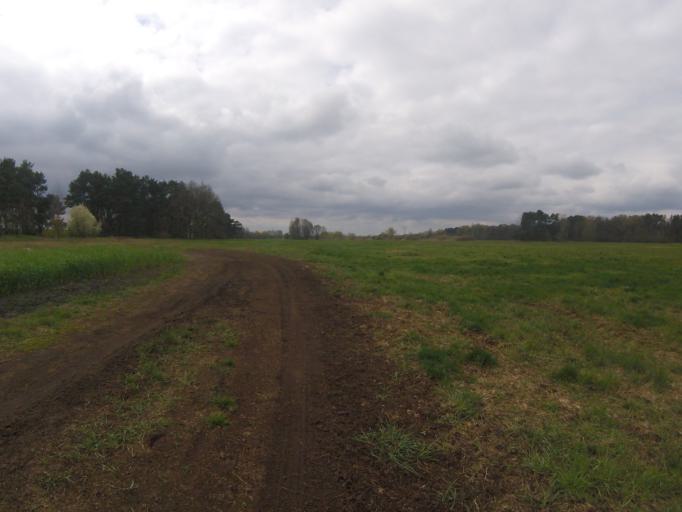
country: DE
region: Brandenburg
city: Konigs Wusterhausen
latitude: 52.2634
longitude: 13.5952
